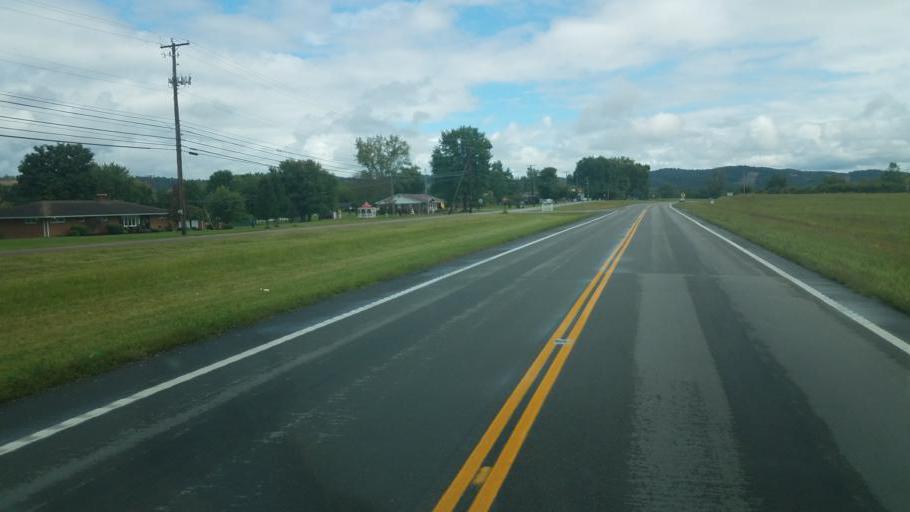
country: US
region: Ohio
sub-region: Scioto County
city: Lucasville
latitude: 38.8801
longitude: -82.9813
